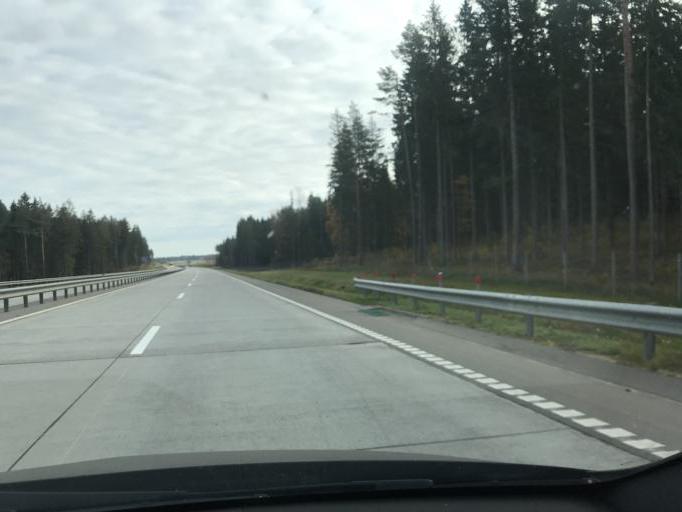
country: BY
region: Minsk
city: Syomkava
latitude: 54.0634
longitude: 27.3723
